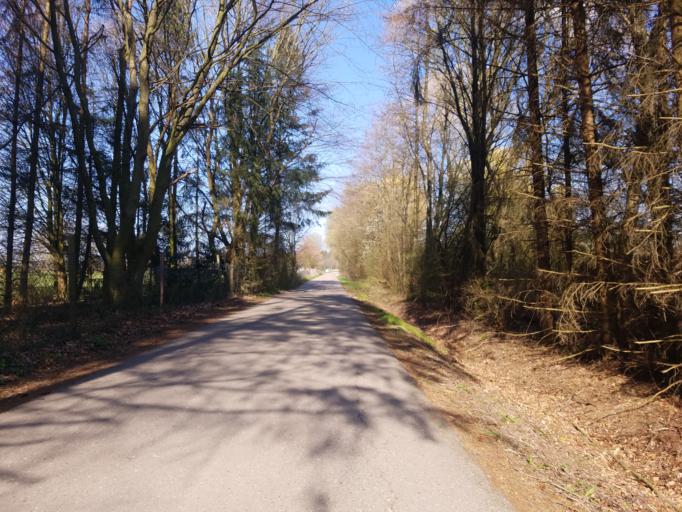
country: DE
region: Baden-Wuerttemberg
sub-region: Karlsruhe Region
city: Schwarzach
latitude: 48.7495
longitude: 8.0625
